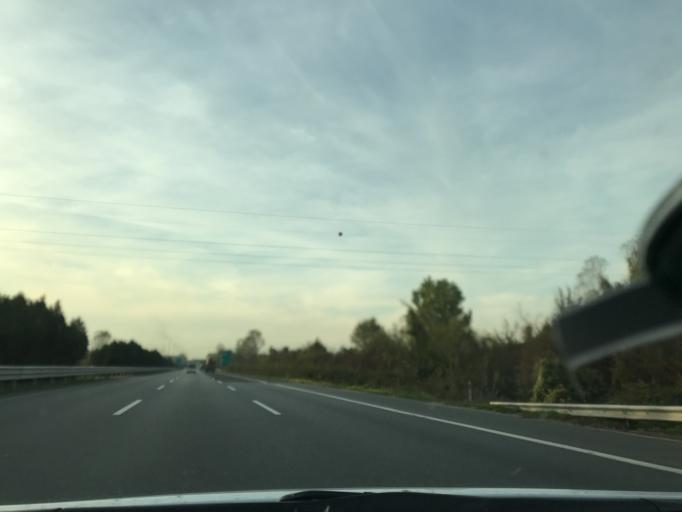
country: TR
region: Duzce
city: Cilimli
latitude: 40.8268
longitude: 31.0537
